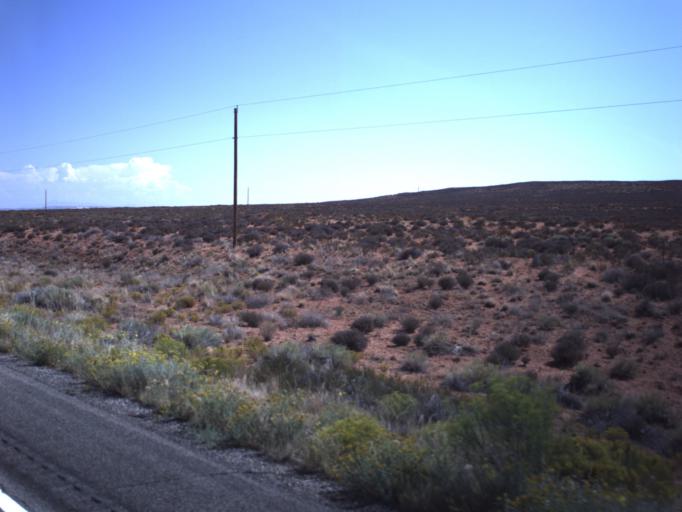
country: US
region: Utah
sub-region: San Juan County
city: Blanding
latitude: 37.0326
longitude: -109.5924
